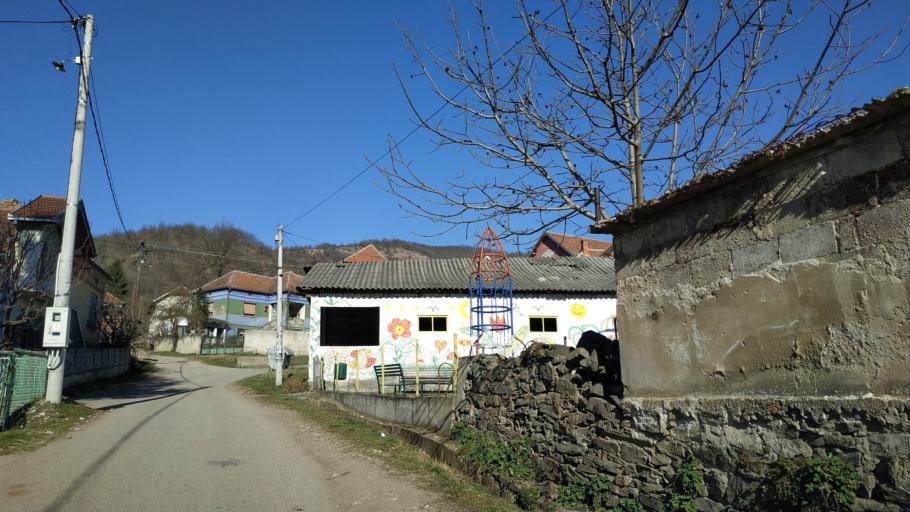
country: RS
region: Central Serbia
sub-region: Nisavski Okrug
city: Aleksinac
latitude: 43.6349
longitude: 21.7189
